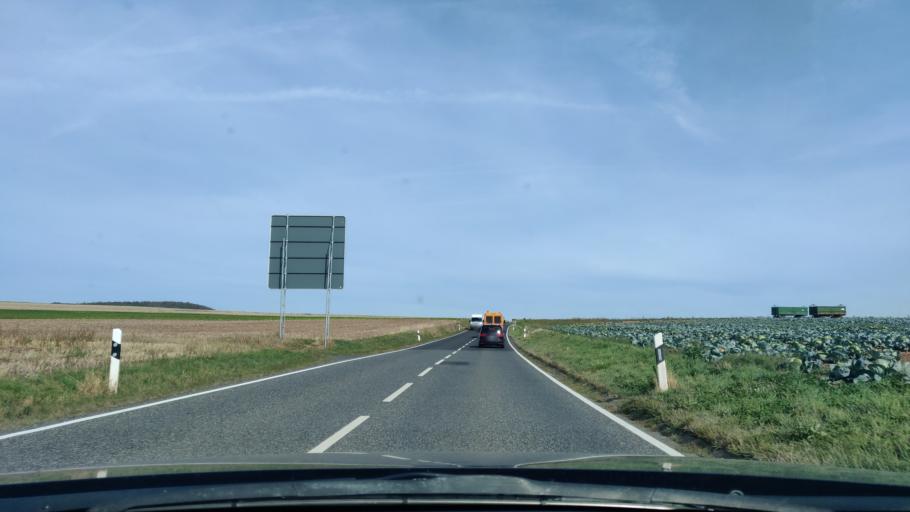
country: DE
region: Hesse
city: Fritzlar
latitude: 51.1668
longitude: 9.2701
